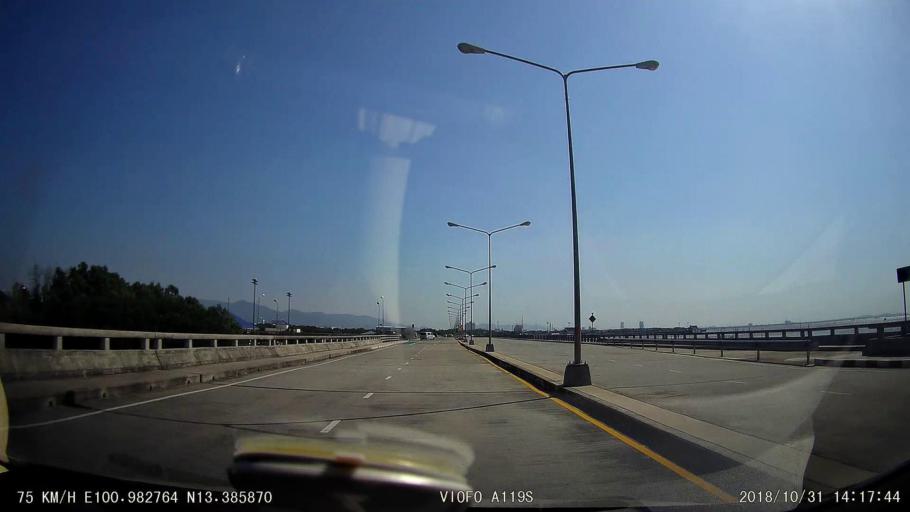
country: TH
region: Chon Buri
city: Chon Buri
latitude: 13.3857
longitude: 100.9828
